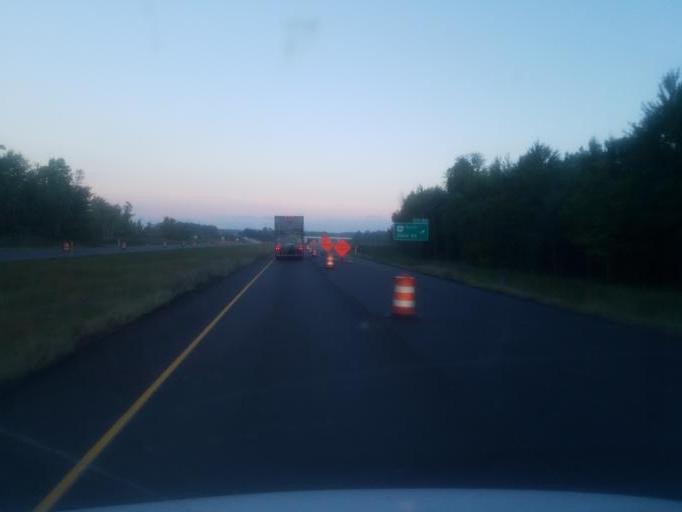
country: US
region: Ohio
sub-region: Ashtabula County
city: Jefferson
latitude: 41.8041
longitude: -80.7534
